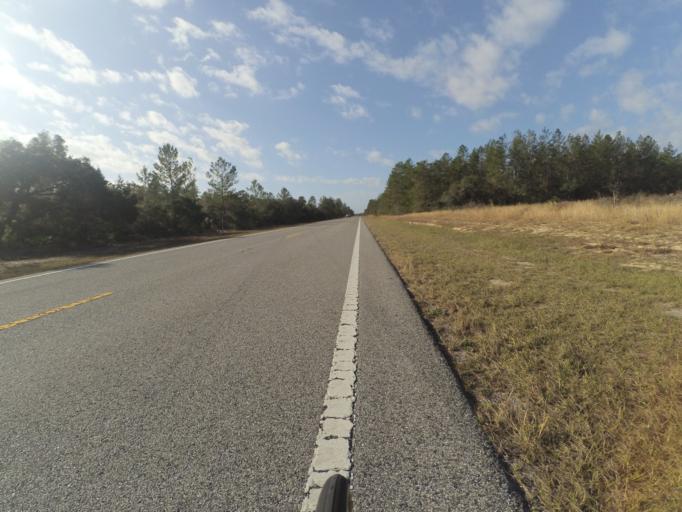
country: US
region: Florida
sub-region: Lake County
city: Astor
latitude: 29.1371
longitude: -81.6004
